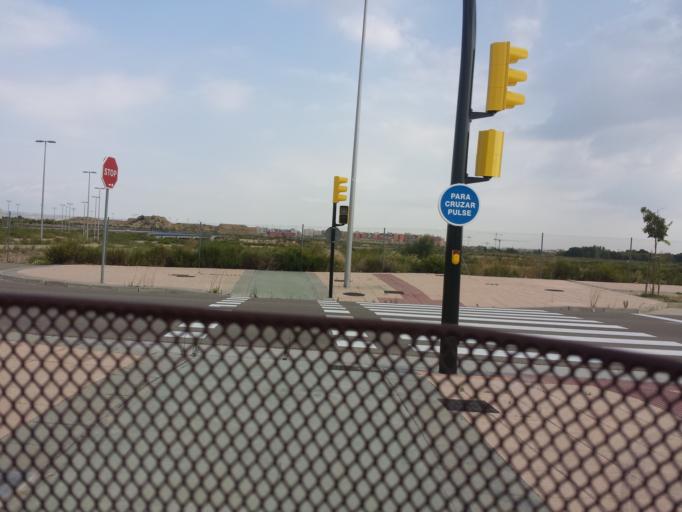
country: ES
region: Aragon
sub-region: Provincia de Zaragoza
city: Montecanal
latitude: 41.6257
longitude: -0.9560
